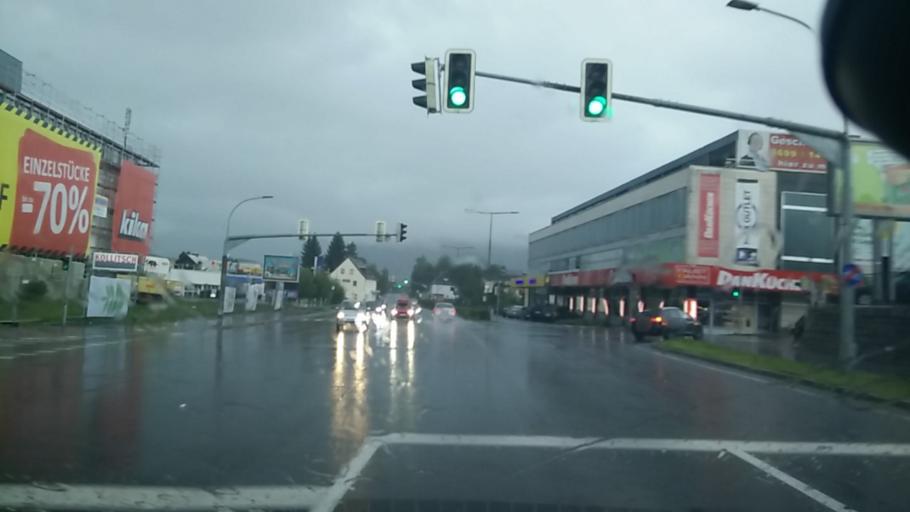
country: AT
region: Carinthia
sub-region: Villach Stadt
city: Villach
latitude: 46.6004
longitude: 13.8396
